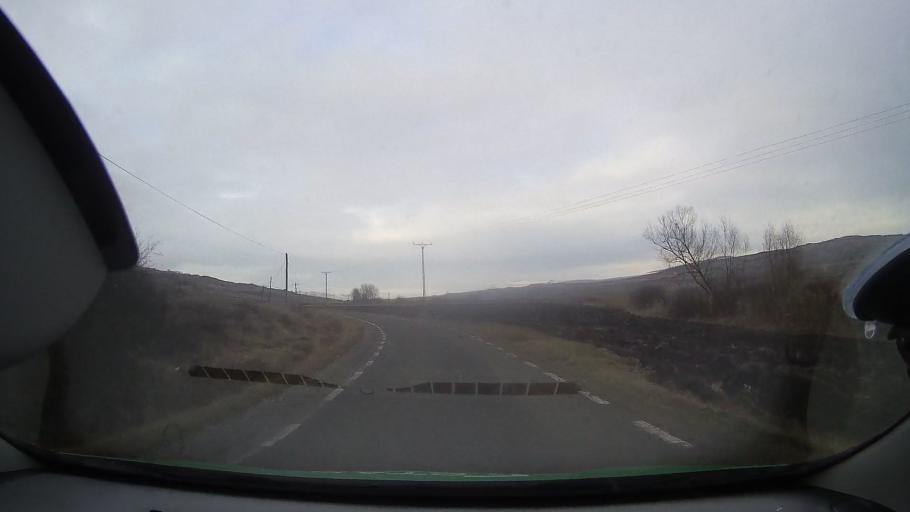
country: RO
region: Mures
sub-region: Comuna Bichis
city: Bichis
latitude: 46.3931
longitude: 24.0903
